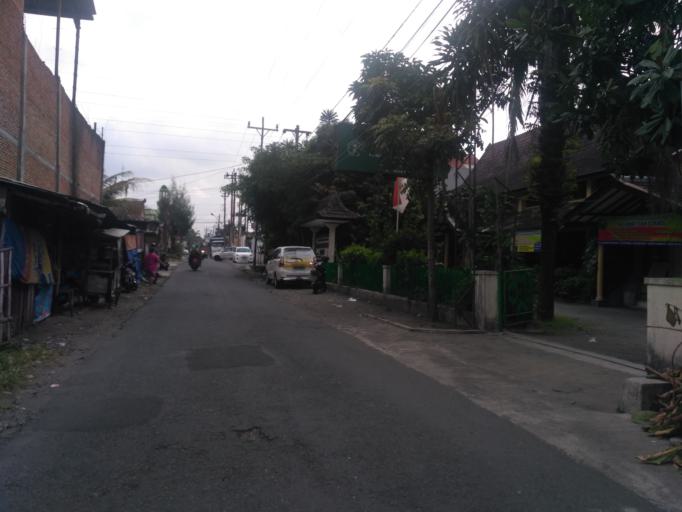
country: ID
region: Daerah Istimewa Yogyakarta
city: Melati
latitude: -7.7561
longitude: 110.3631
